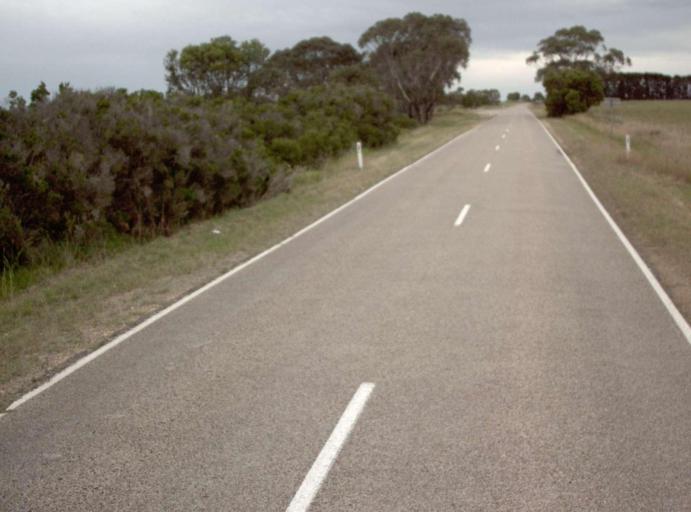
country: AU
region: Victoria
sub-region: East Gippsland
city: Bairnsdale
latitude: -37.9489
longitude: 147.5215
